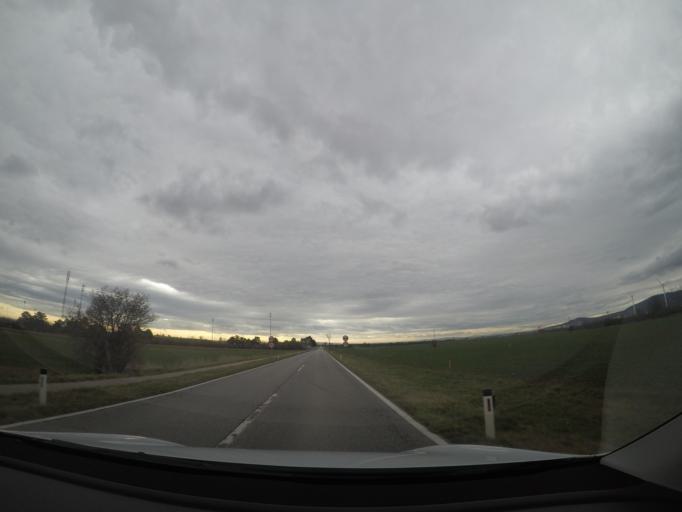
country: AT
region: Lower Austria
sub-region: Politischer Bezirk Modling
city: Vosendorf
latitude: 48.1173
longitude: 16.3327
